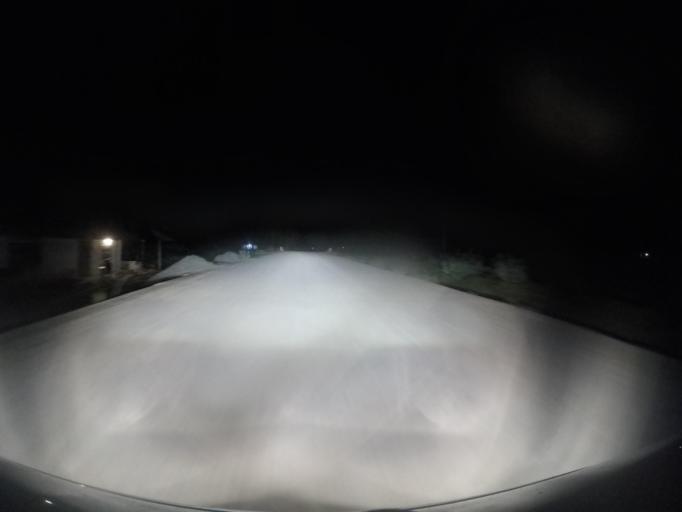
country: TL
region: Viqueque
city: Viqueque
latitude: -8.8060
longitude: 126.5448
